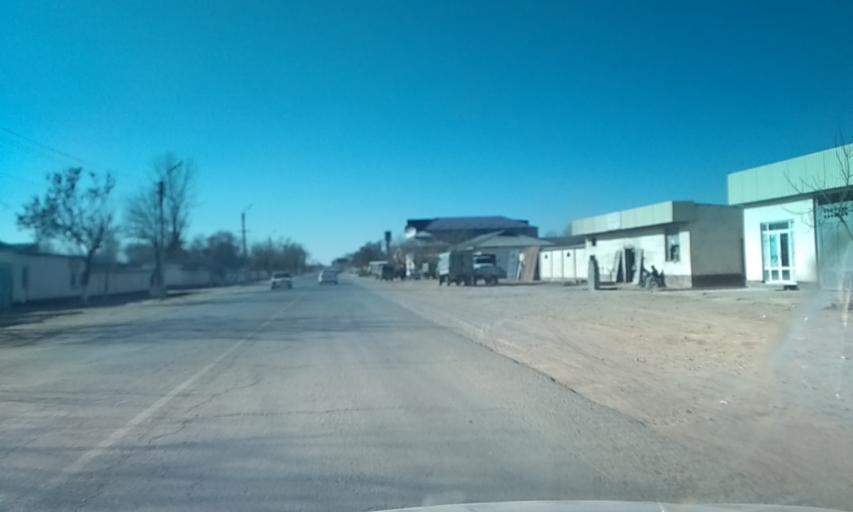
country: UZ
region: Sirdaryo
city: Guliston
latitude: 40.4941
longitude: 68.8054
